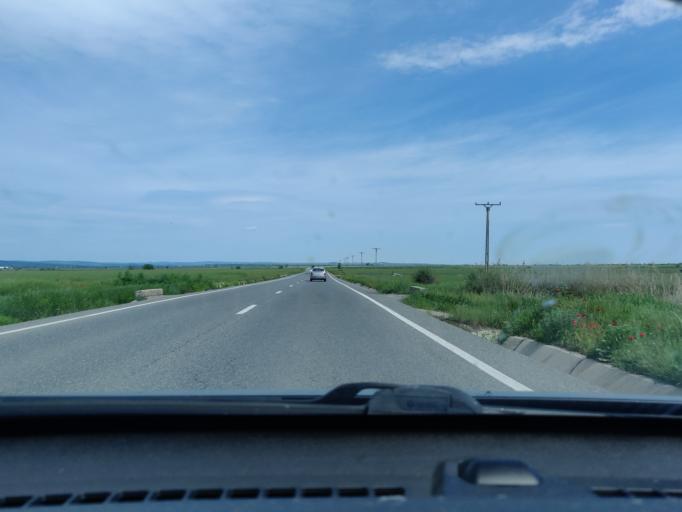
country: RO
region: Vrancea
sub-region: Oras Odobesti
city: Unirea
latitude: 45.7684
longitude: 27.1210
